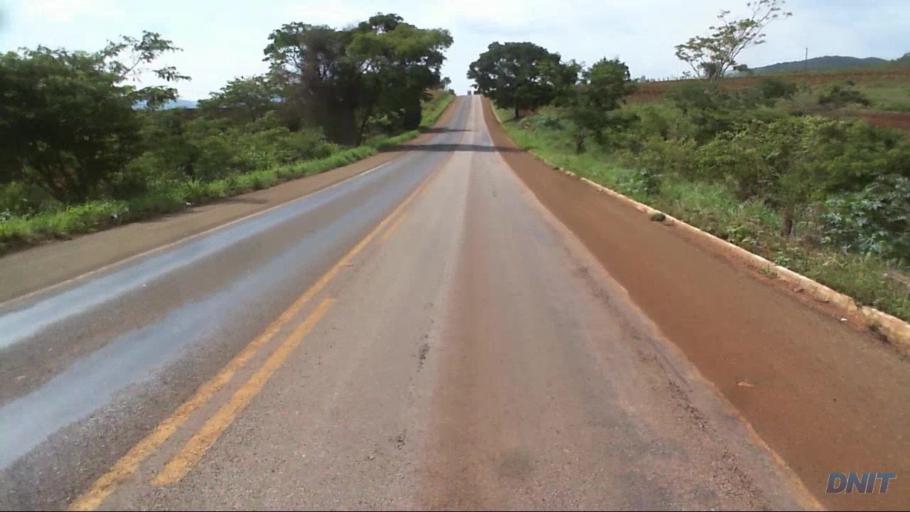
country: BR
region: Goias
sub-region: Barro Alto
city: Barro Alto
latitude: -14.9967
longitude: -48.9063
